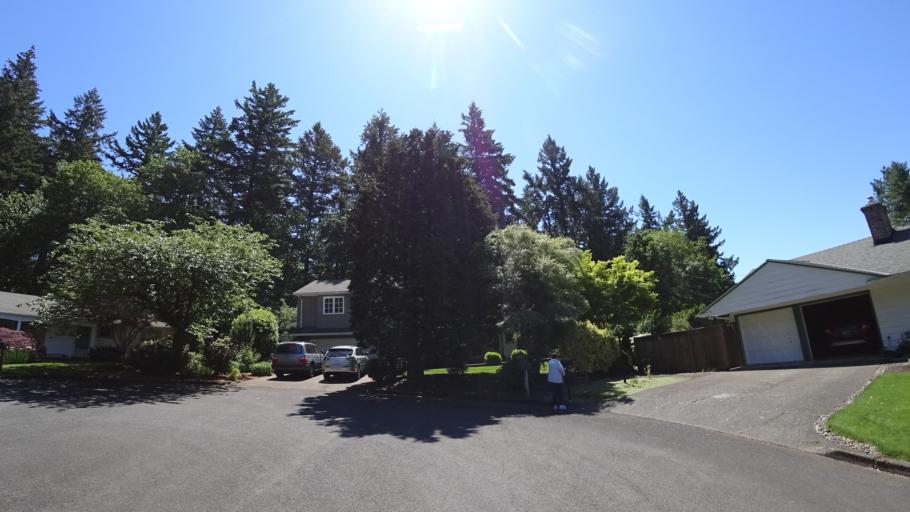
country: US
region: Oregon
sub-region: Washington County
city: Raleigh Hills
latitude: 45.4886
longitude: -122.7175
